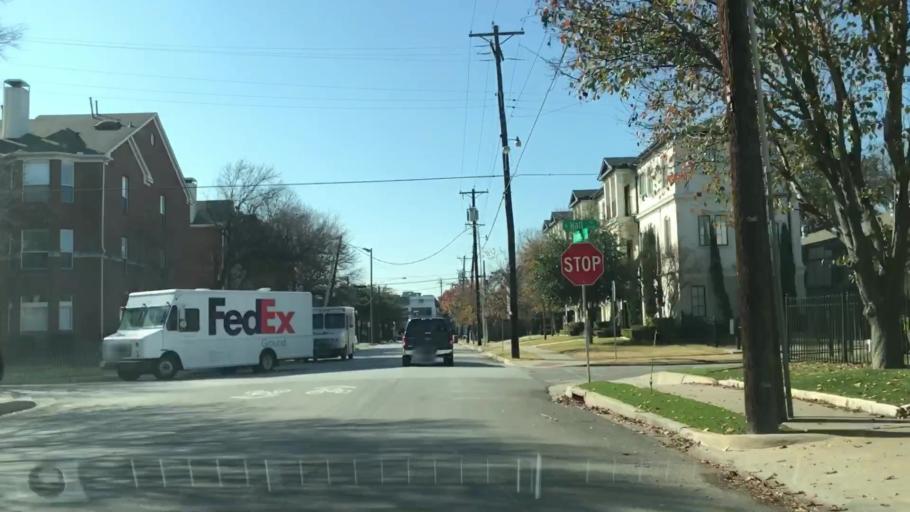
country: US
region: Texas
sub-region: Dallas County
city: Highland Park
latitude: 32.8122
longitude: -96.8097
